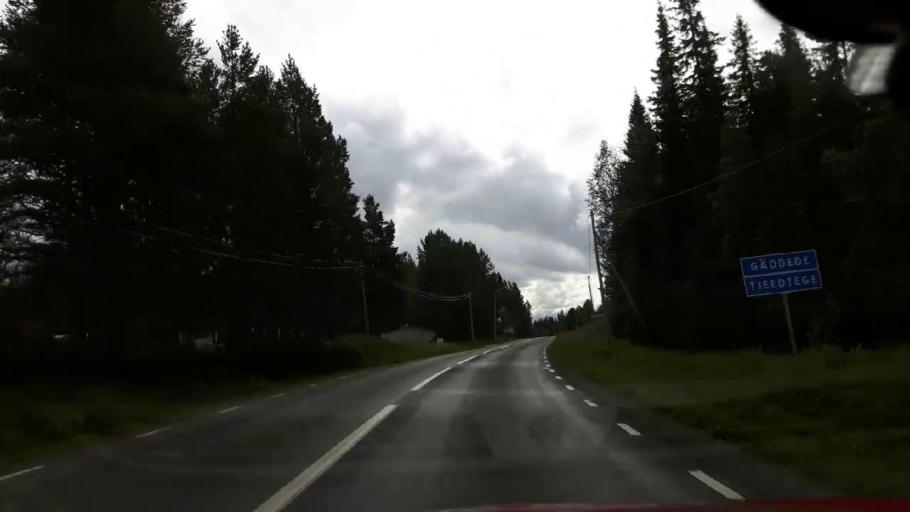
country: NO
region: Nord-Trondelag
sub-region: Lierne
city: Sandvika
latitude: 64.5079
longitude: 14.1577
